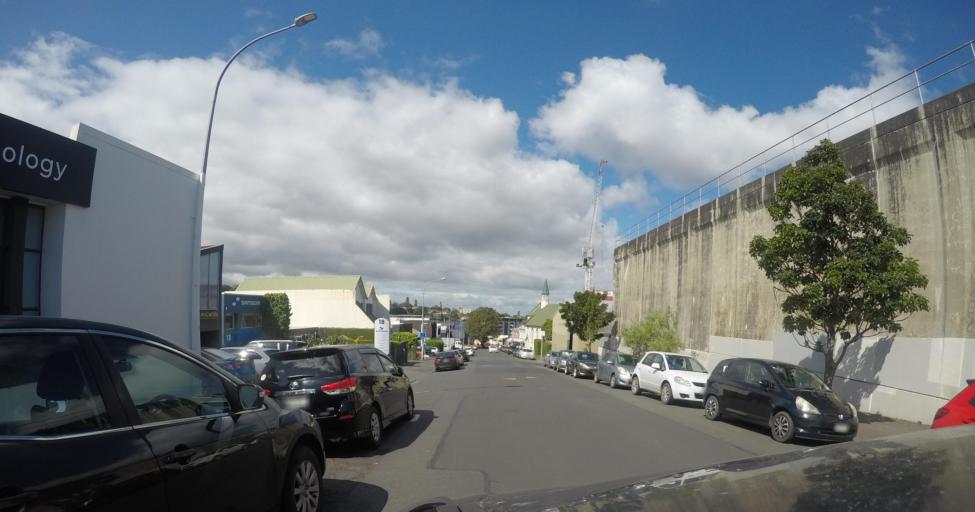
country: NZ
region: Auckland
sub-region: Auckland
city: Auckland
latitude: -36.8651
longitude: 174.7623
